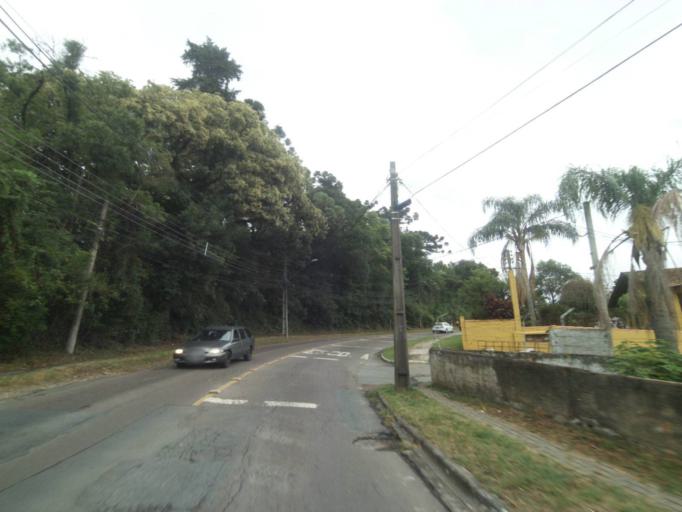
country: BR
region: Parana
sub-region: Curitiba
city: Curitiba
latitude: -25.4506
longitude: -49.3166
